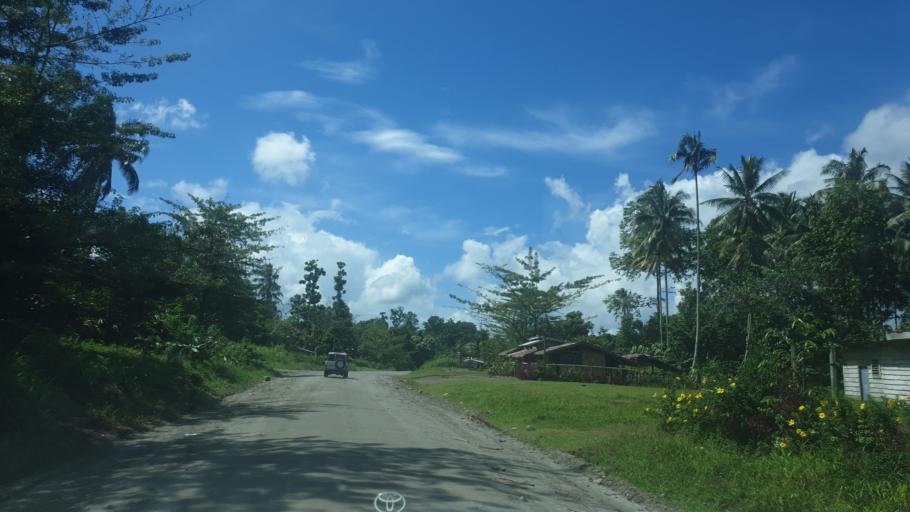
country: PG
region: Bougainville
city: Panguna
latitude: -6.6601
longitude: 155.4455
